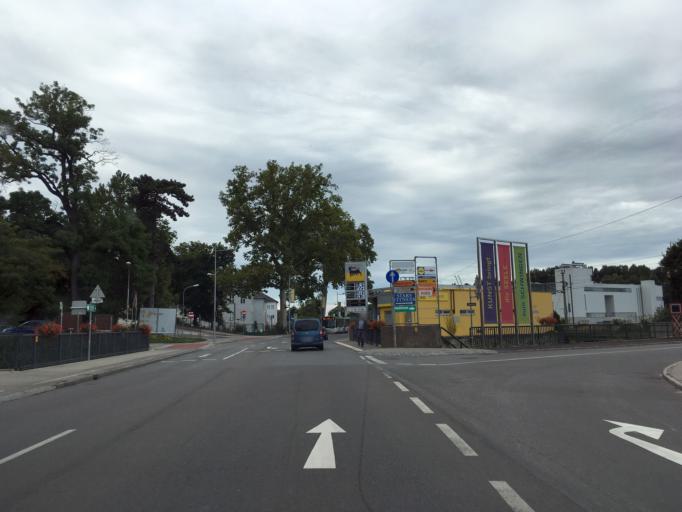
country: AT
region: Lower Austria
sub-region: Politischer Bezirk Wien-Umgebung
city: Klosterneuburg
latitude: 48.2995
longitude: 16.3329
